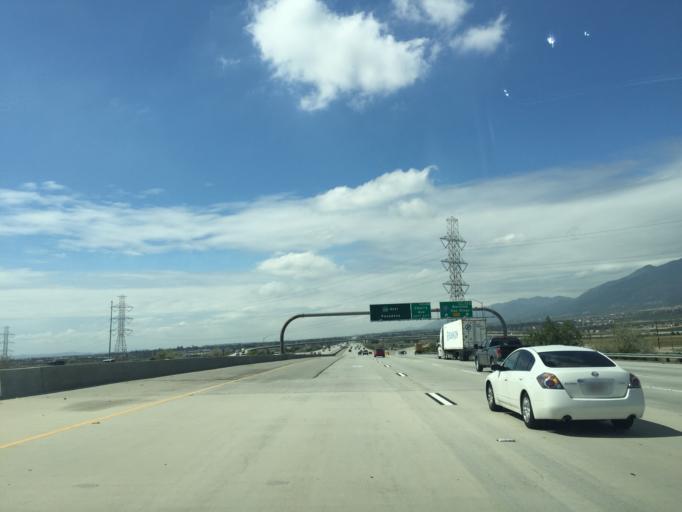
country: US
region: California
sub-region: San Bernardino County
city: Fontana
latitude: 34.1365
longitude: -117.4796
